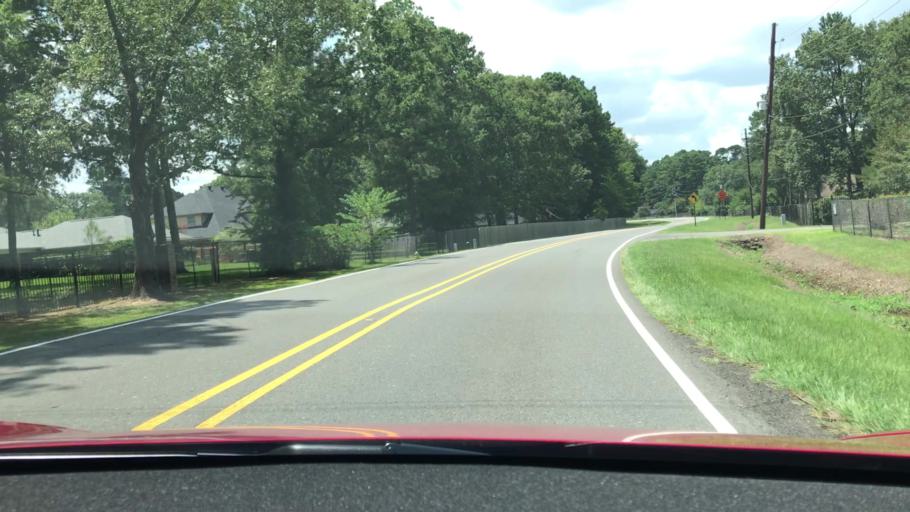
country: US
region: Louisiana
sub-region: De Soto Parish
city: Stonewall
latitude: 32.3667
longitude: -93.7004
